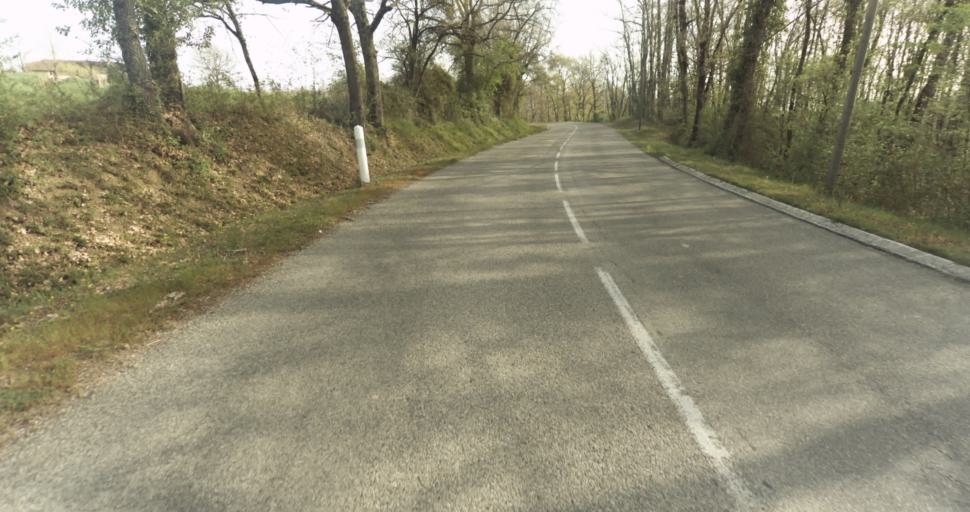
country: FR
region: Midi-Pyrenees
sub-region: Departement du Tarn-et-Garonne
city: Moissac
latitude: 44.1477
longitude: 1.1000
